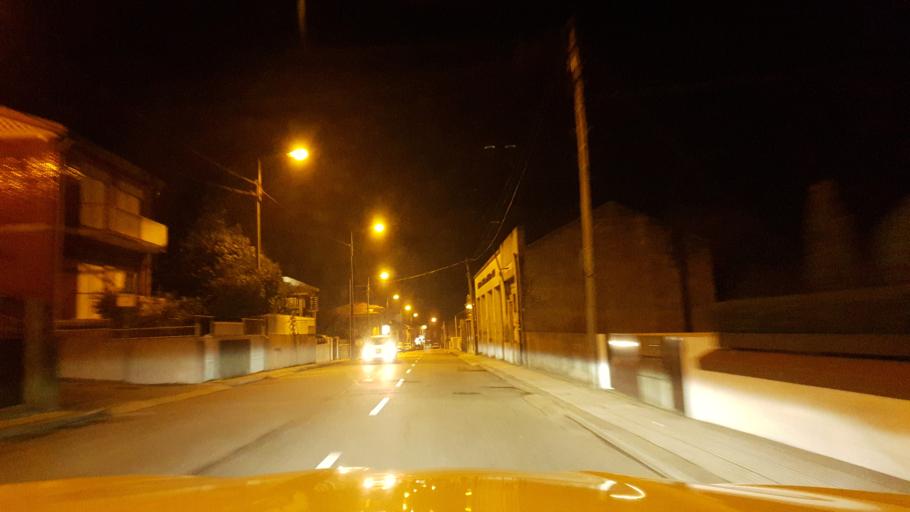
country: PT
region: Porto
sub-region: Maia
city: Leca do Bailio
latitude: 41.2141
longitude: -8.6349
